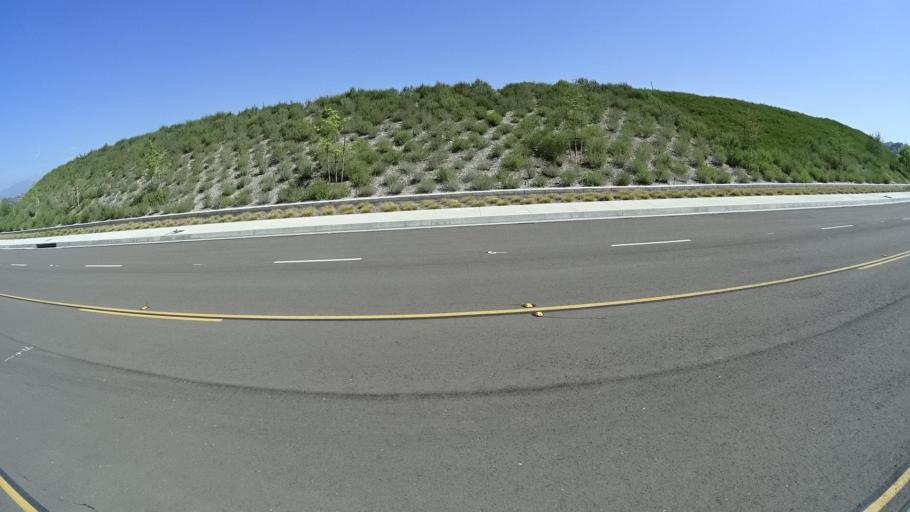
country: US
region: California
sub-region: Los Angeles County
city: Walnut
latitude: 34.0037
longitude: -117.8382
